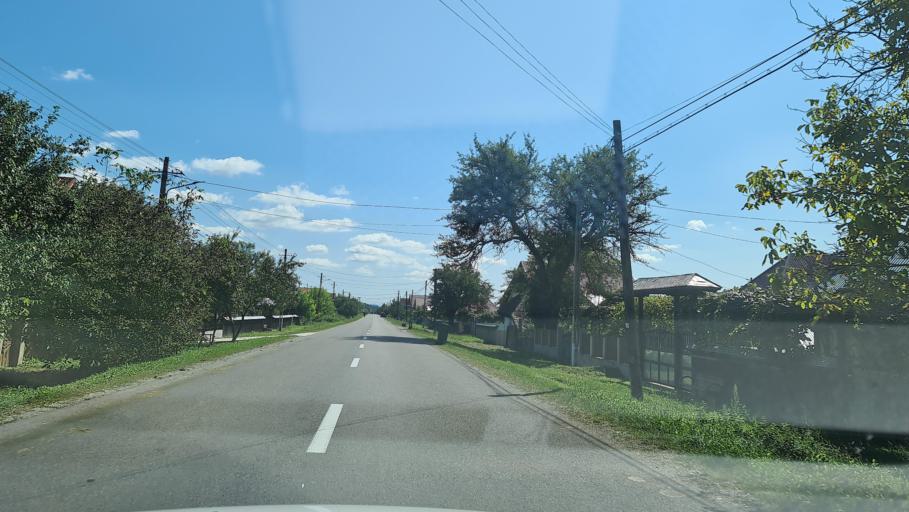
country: RO
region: Bacau
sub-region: Comuna Balcani
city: Balcani
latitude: 46.6445
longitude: 26.5681
